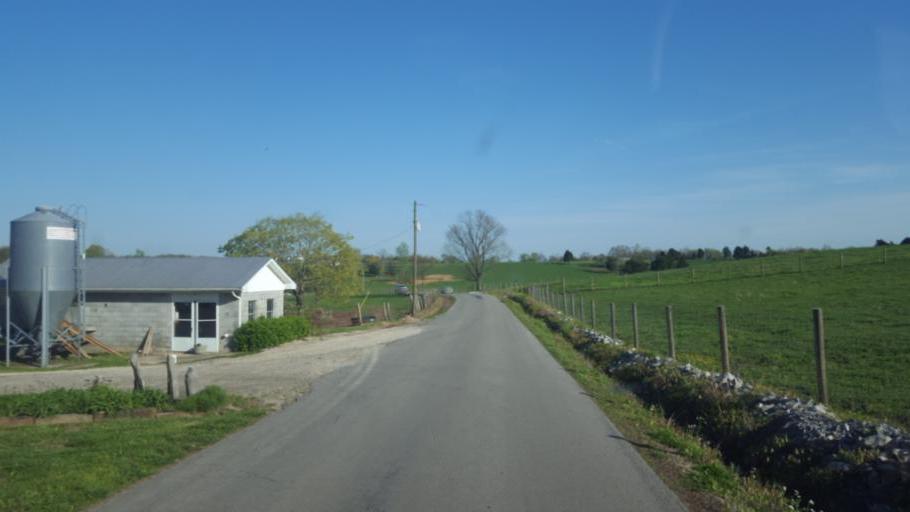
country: US
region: Kentucky
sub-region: Barren County
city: Cave City
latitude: 37.1696
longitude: -85.9876
